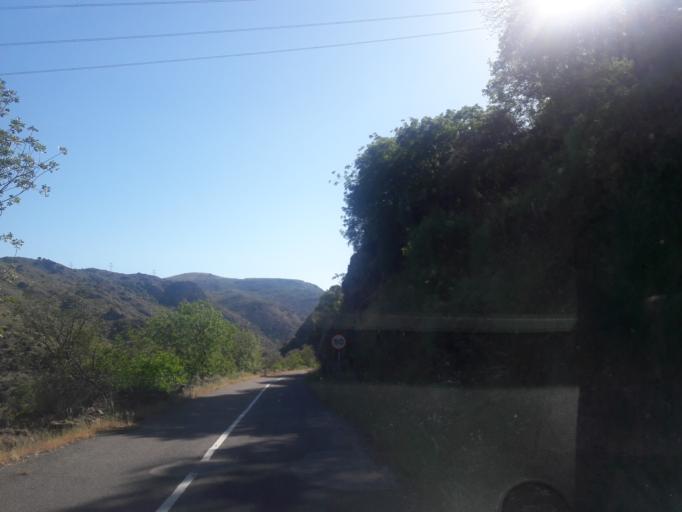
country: ES
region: Castille and Leon
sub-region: Provincia de Salamanca
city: Saucelle
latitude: 41.0229
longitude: -6.7457
